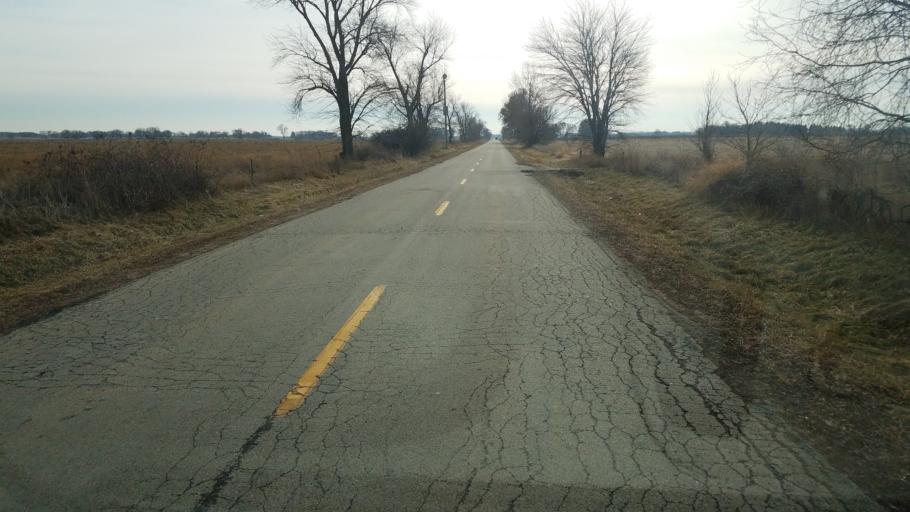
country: US
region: Illinois
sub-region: McHenry County
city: Marengo
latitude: 42.2498
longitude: -88.6524
